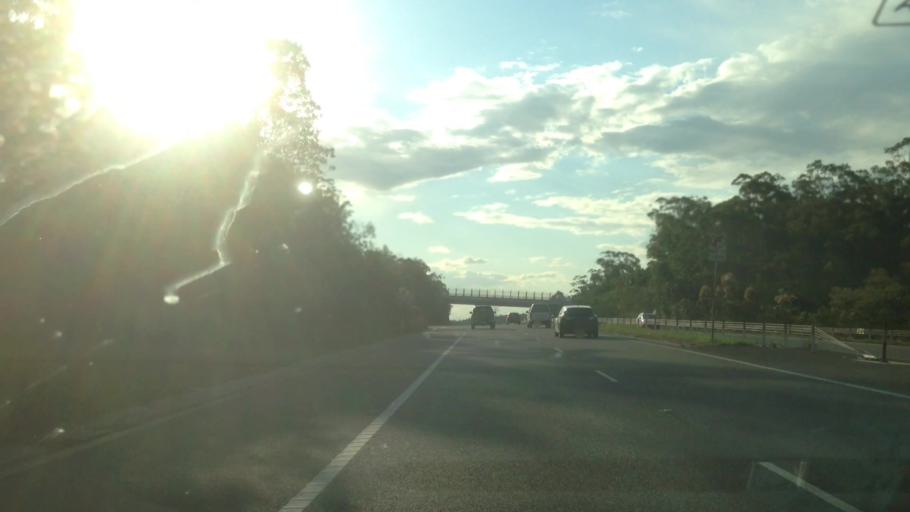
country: AU
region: New South Wales
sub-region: Lake Macquarie Shire
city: Holmesville
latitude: -32.8841
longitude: 151.5908
